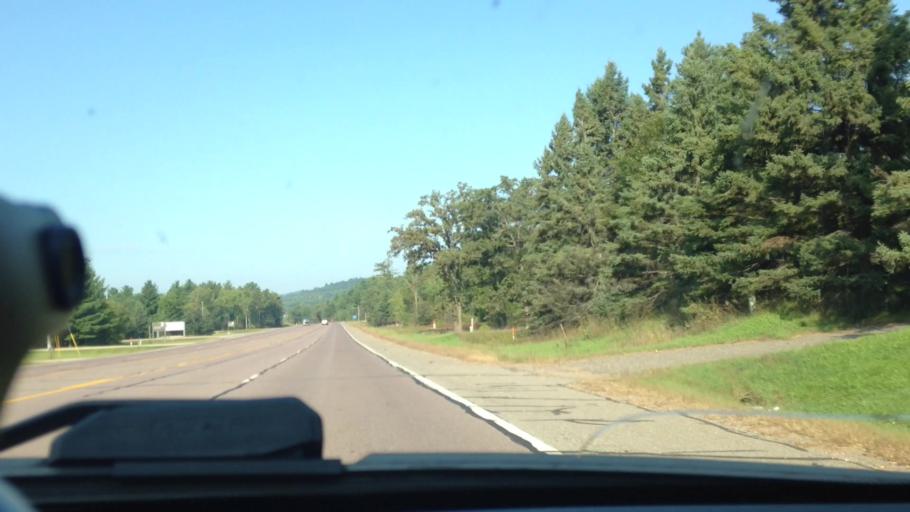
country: US
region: Michigan
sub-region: Dickinson County
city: Quinnesec
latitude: 45.8028
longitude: -87.9618
